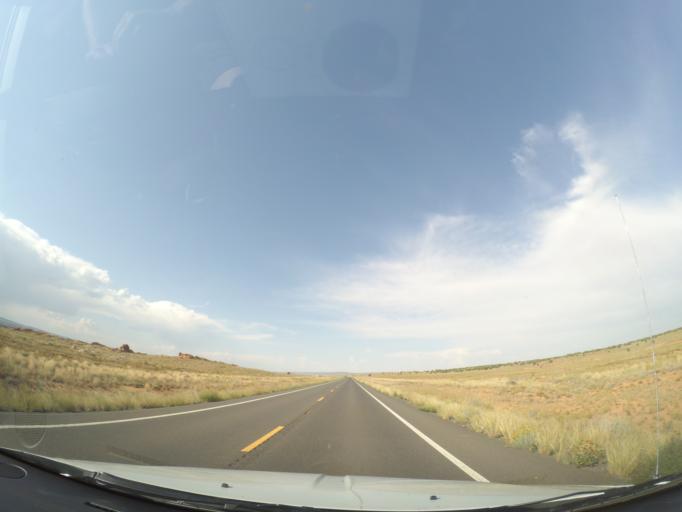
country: US
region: Arizona
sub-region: Coconino County
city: Tuba City
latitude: 36.3502
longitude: -111.4258
